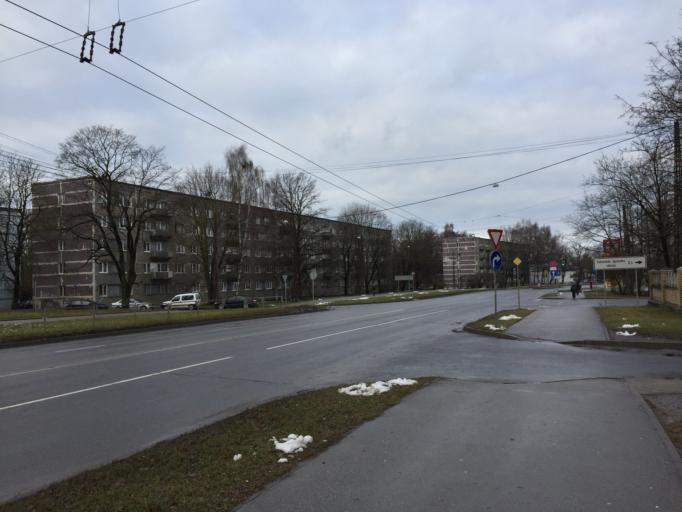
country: LV
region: Marupe
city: Marupe
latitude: 56.9573
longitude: 24.0525
